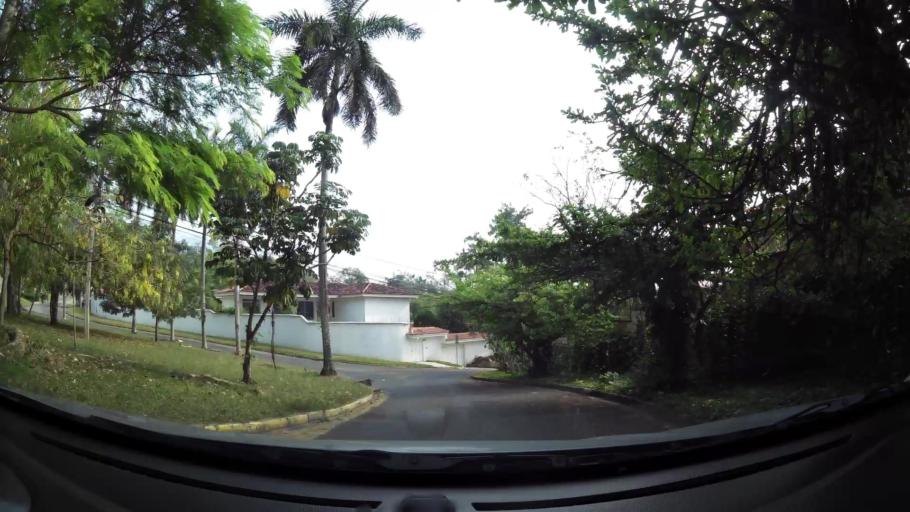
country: HN
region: Cortes
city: El Zapotal del Norte
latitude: 15.5129
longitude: -88.0500
